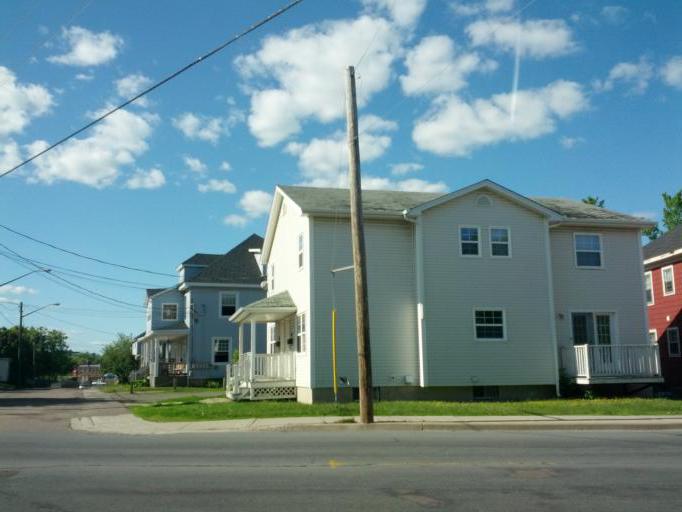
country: CA
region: New Brunswick
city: Moncton
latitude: 46.0944
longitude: -64.7770
